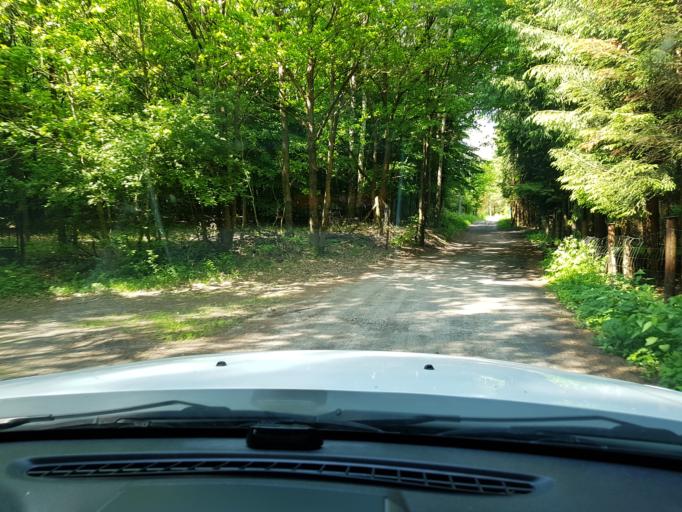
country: PL
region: West Pomeranian Voivodeship
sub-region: Powiat drawski
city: Drawsko Pomorskie
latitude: 53.5468
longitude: 15.7139
